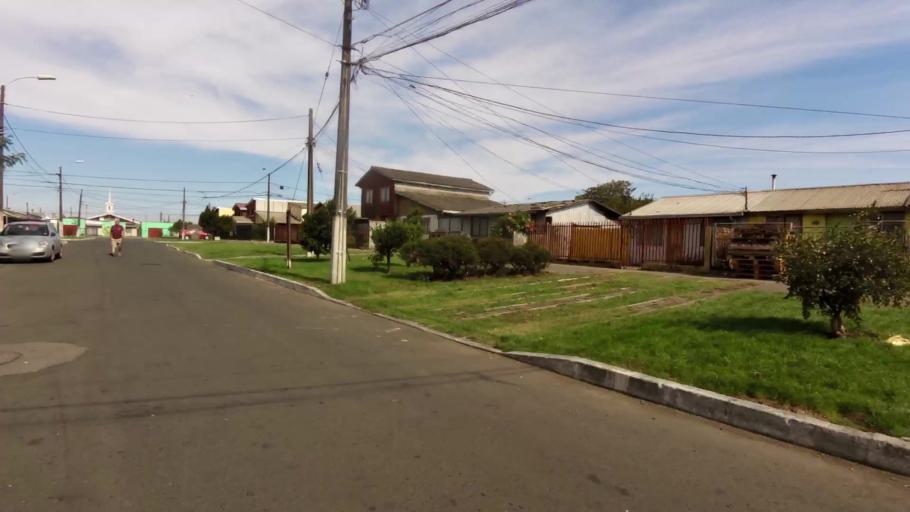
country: CL
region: Biobio
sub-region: Provincia de Concepcion
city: Talcahuano
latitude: -36.7794
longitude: -73.1066
